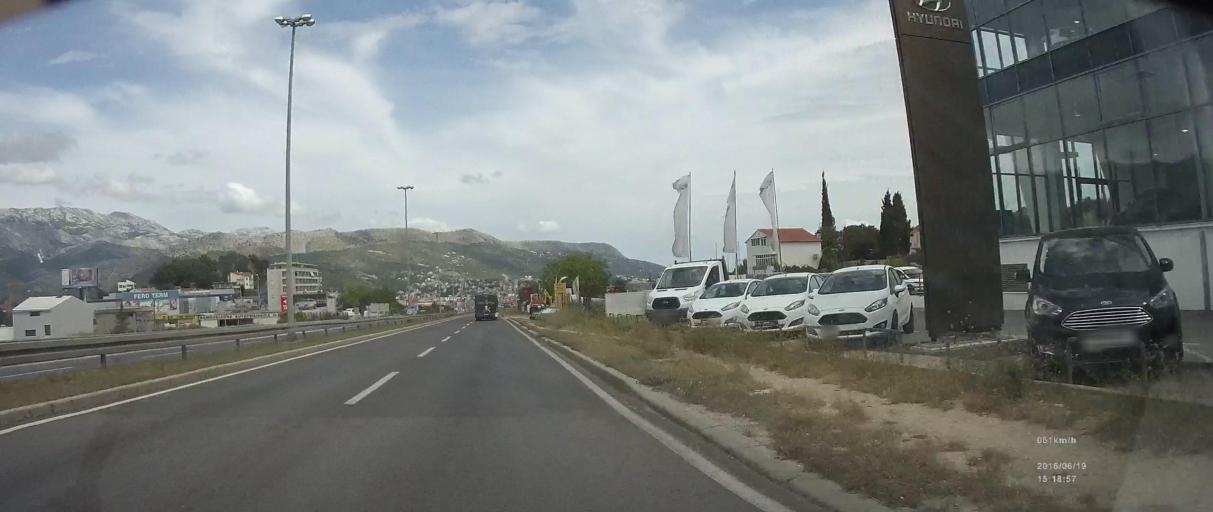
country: HR
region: Splitsko-Dalmatinska
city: Kamen
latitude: 43.5080
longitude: 16.4994
